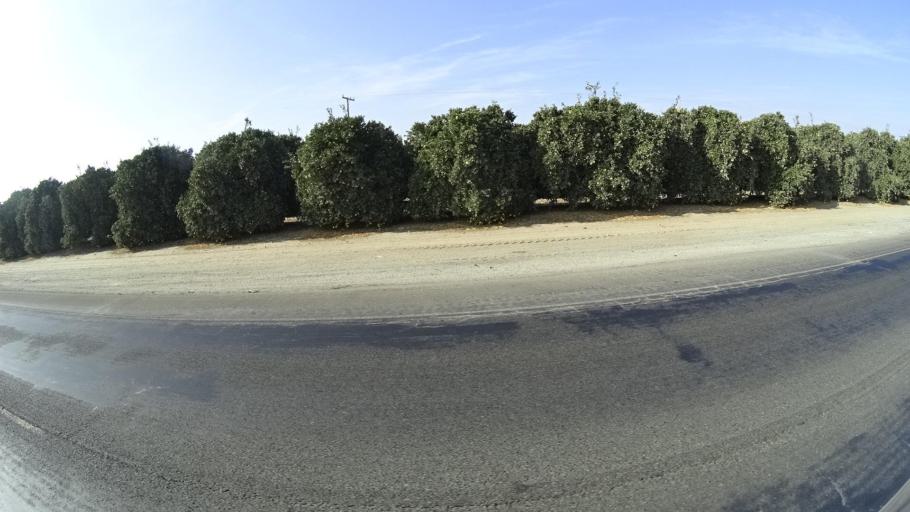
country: US
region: California
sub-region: Kern County
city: McFarland
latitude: 35.6998
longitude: -119.1708
